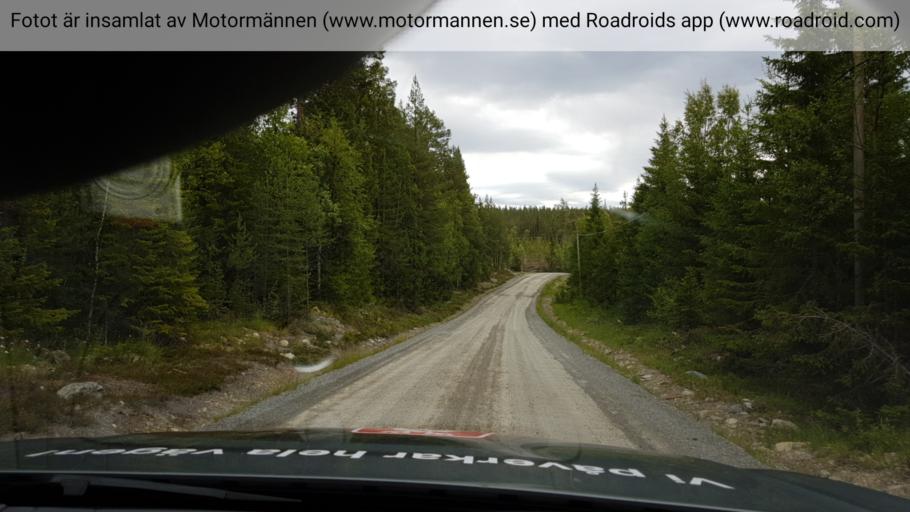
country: SE
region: Jaemtland
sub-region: Bergs Kommun
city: Hoverberg
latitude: 62.7894
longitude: 13.8213
